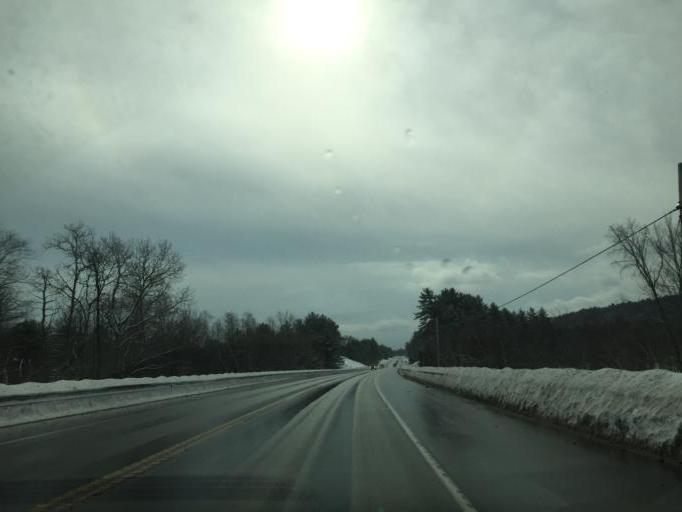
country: US
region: New Hampshire
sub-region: Carroll County
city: Sanbornville
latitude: 43.5415
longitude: -71.0333
